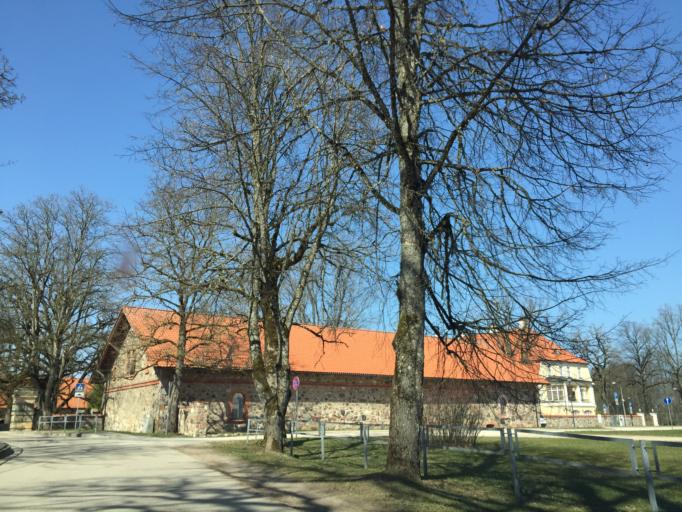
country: LV
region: Malpils
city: Malpils
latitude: 57.0053
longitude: 24.9493
